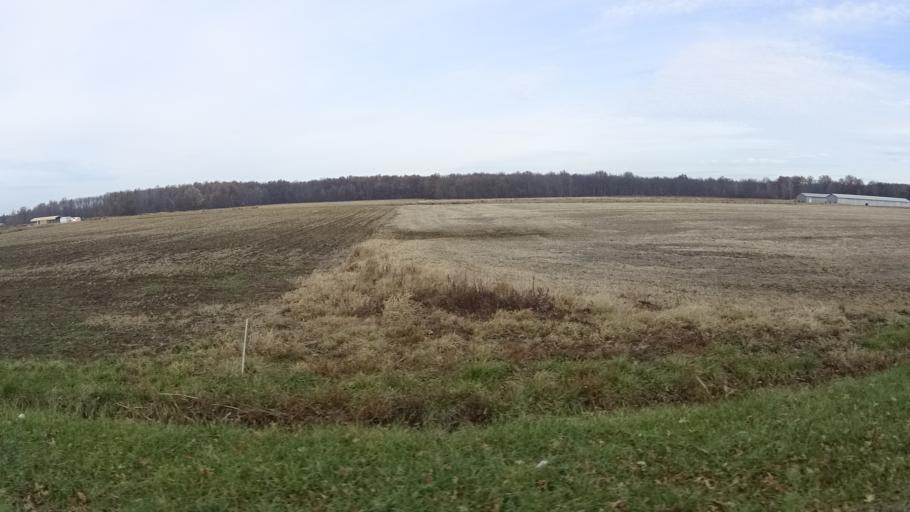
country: US
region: Ohio
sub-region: Lorain County
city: Eaton Estates
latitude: 41.2600
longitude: -81.9929
